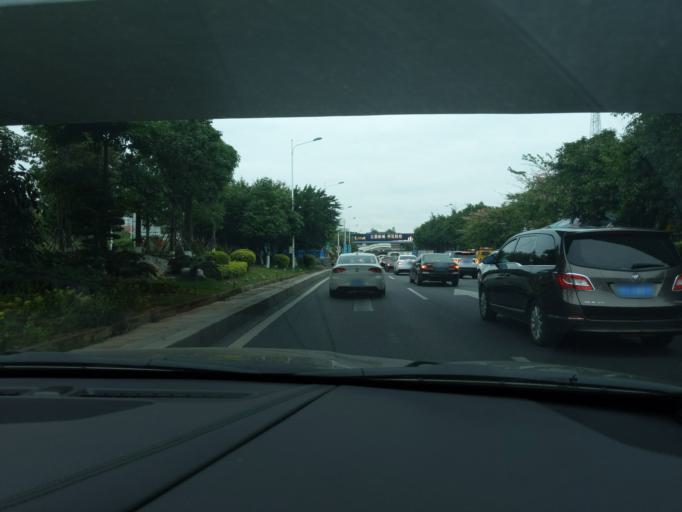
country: CN
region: Fujian
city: Liuwudian
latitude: 24.5147
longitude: 118.1788
